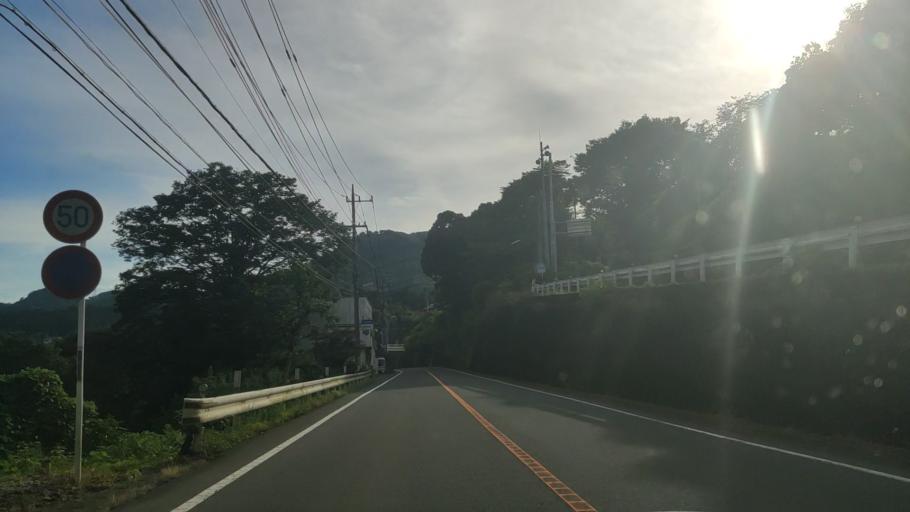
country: JP
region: Gunma
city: Omamacho-omama
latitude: 36.4824
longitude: 139.2602
